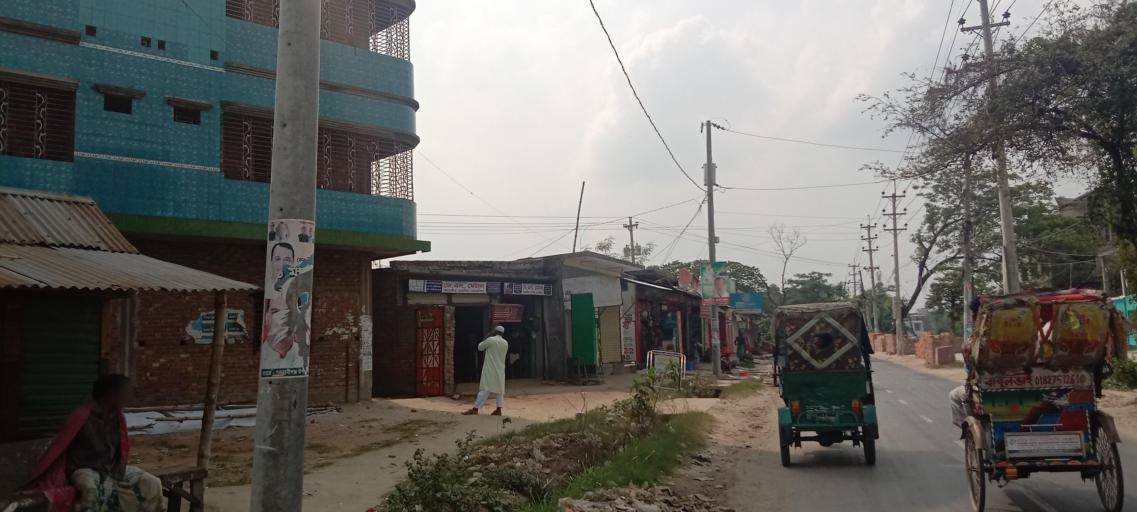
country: BD
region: Dhaka
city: Azimpur
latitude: 23.7154
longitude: 90.3551
